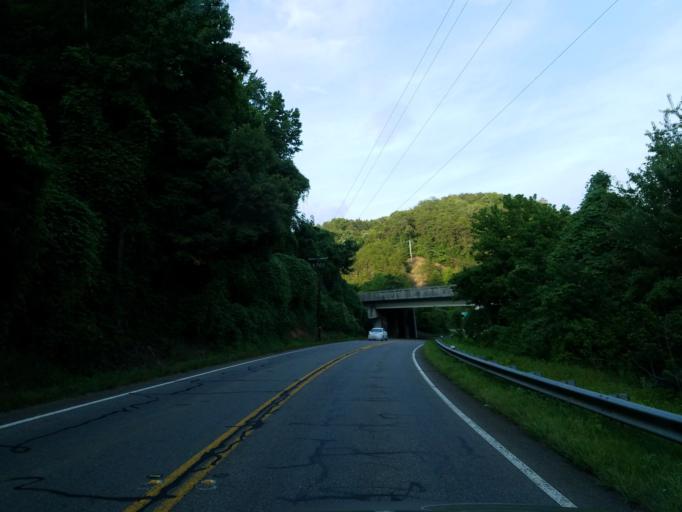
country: US
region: Georgia
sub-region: Gilmer County
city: Ellijay
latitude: 34.6888
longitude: -84.4688
